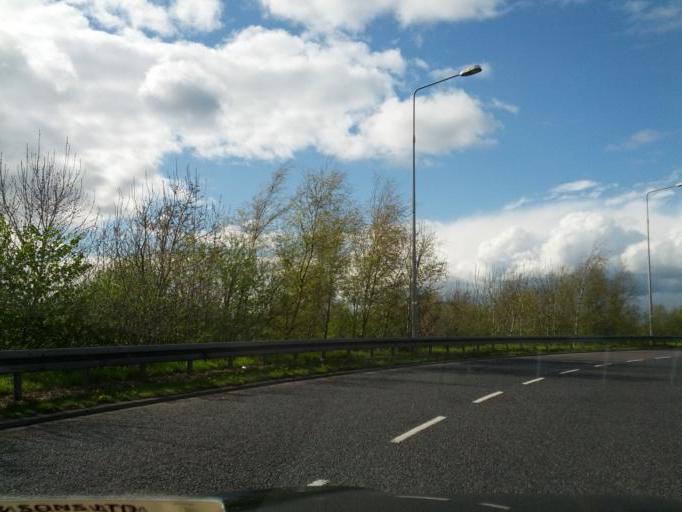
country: IE
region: Leinster
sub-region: Kildare
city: Kilcock
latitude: 53.4013
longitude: -6.6910
